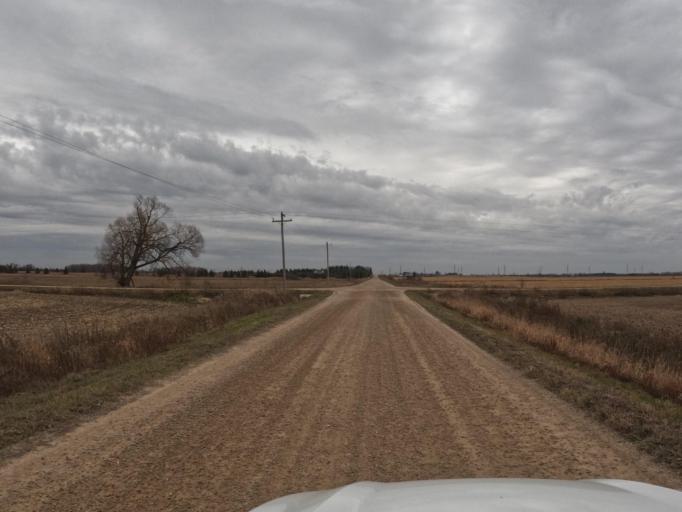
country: CA
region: Ontario
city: Shelburne
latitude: 44.0115
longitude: -80.3896
